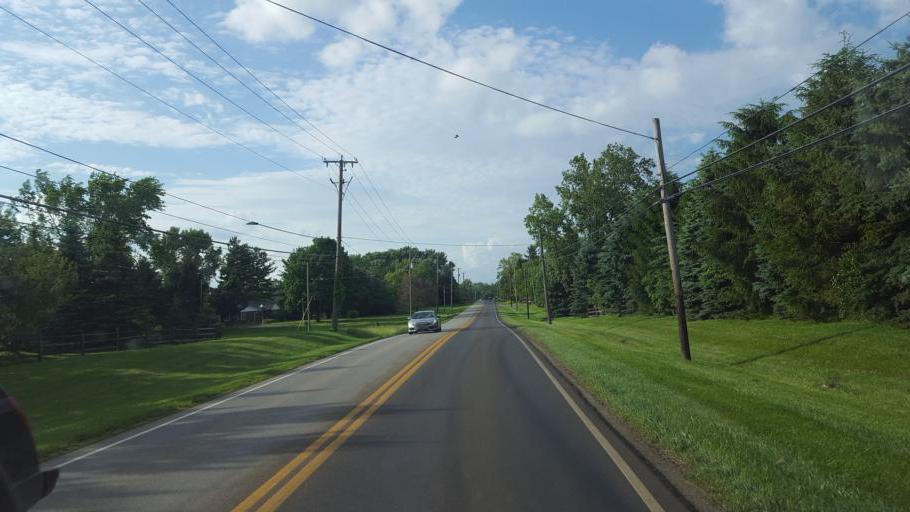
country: US
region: Ohio
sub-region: Delaware County
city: Lewis Center
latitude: 40.1908
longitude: -82.9910
